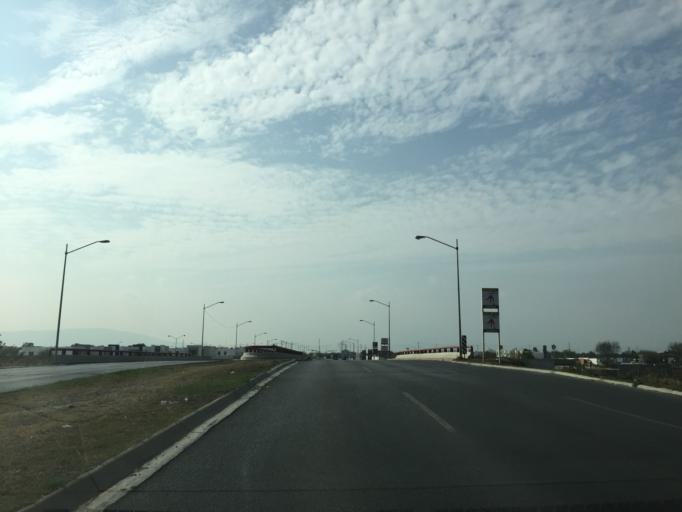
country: MX
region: Nuevo Leon
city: Apodaca
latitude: 25.7765
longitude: -100.2093
